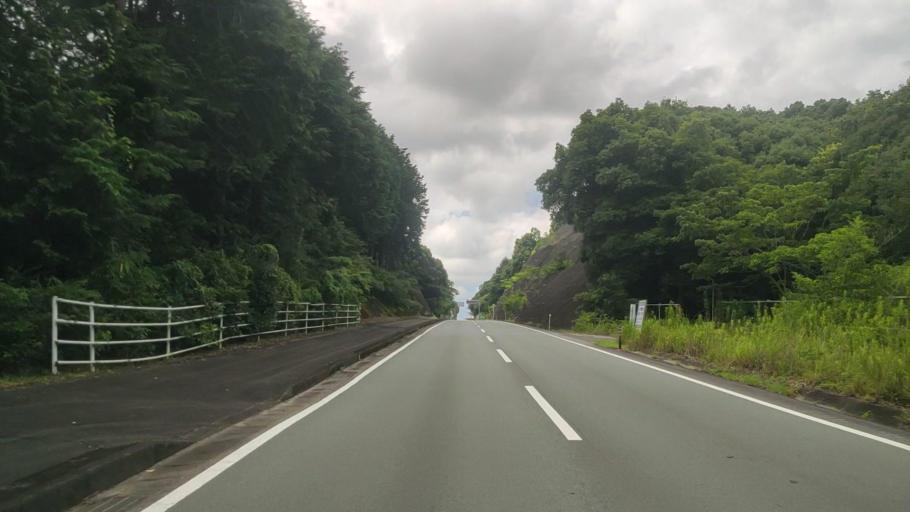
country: JP
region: Mie
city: Toba
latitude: 34.3827
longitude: 136.7943
